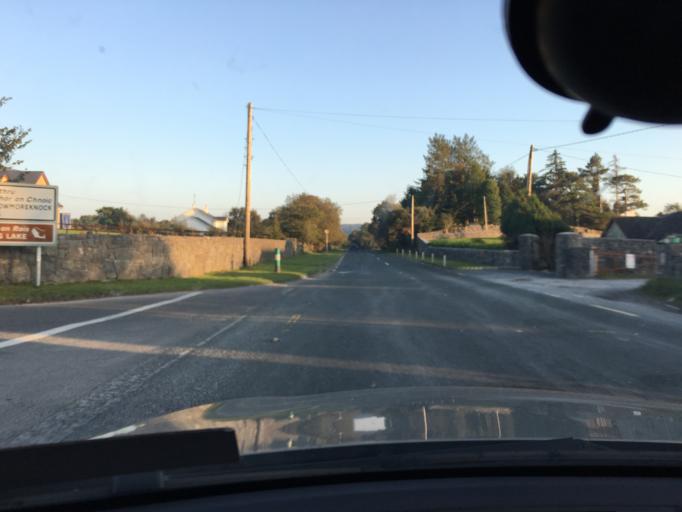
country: IE
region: Connaught
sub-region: County Galway
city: Moycullen
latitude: 53.3558
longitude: -9.2074
